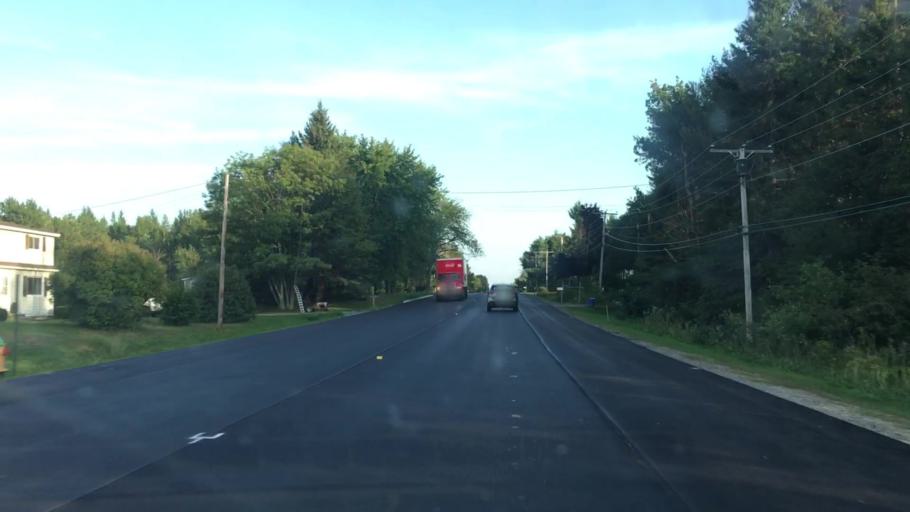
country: US
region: Maine
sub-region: Penobscot County
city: Hampden
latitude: 44.7639
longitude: -68.8513
